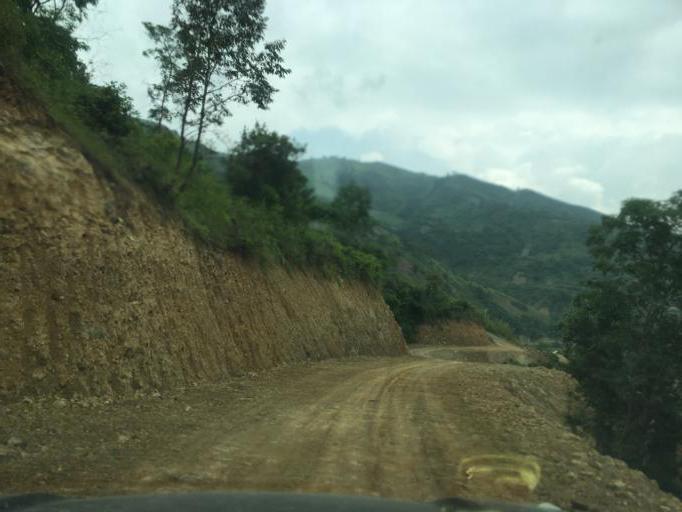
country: CN
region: Guangxi Zhuangzu Zizhiqu
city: Tongle
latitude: 25.1227
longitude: 106.4146
